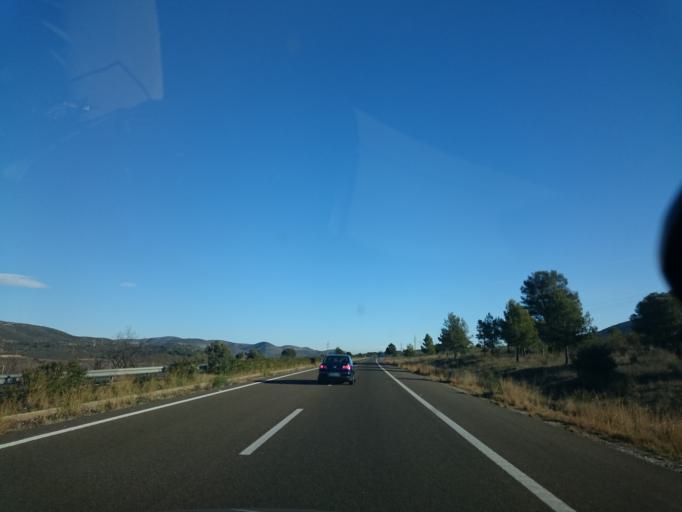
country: ES
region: Valencia
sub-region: Provincia de Castello
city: Alcala de Xivert
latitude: 40.3293
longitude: 0.2595
